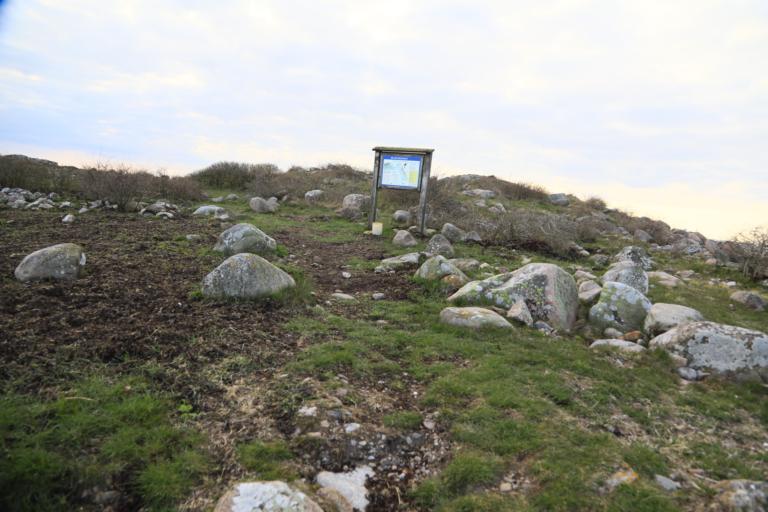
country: SE
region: Halland
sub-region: Varbergs Kommun
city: Traslovslage
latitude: 57.0660
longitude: 12.2491
